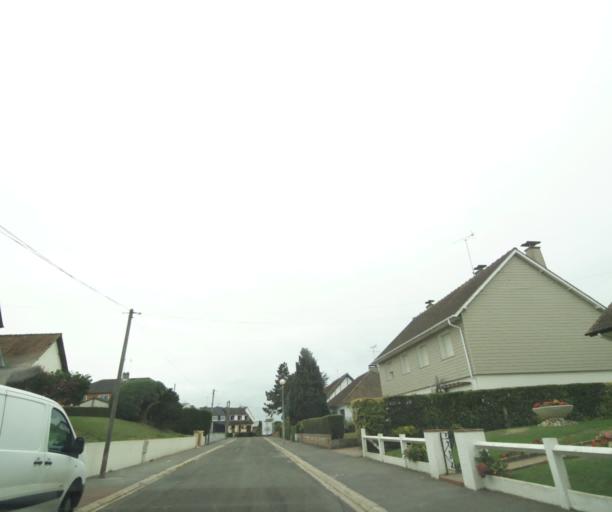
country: FR
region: Nord-Pas-de-Calais
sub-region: Departement du Pas-de-Calais
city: Etaples
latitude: 50.5229
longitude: 1.6348
